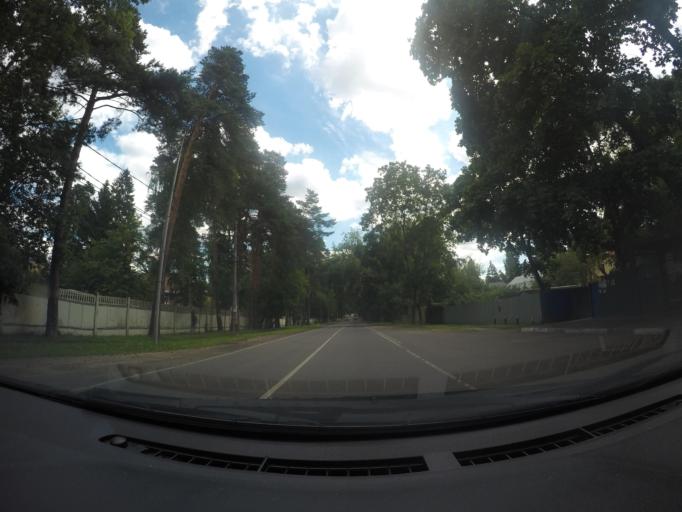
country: RU
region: Moskovskaya
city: Kraskovo
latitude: 55.6542
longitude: 37.9923
